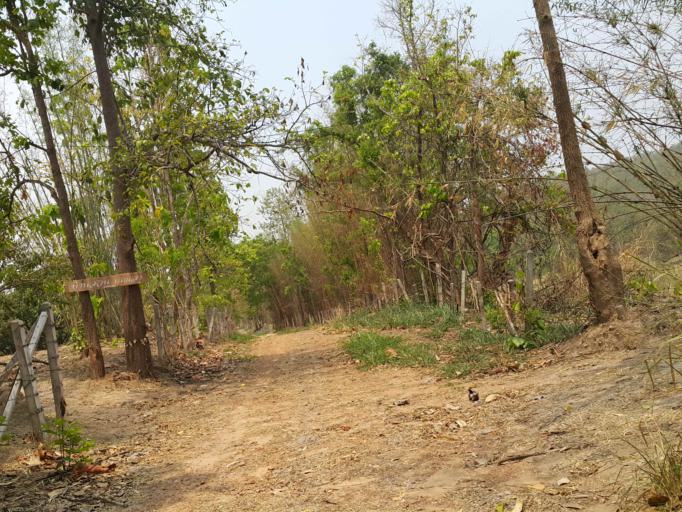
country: TH
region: Chiang Mai
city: San Sai
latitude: 18.9379
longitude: 99.0380
